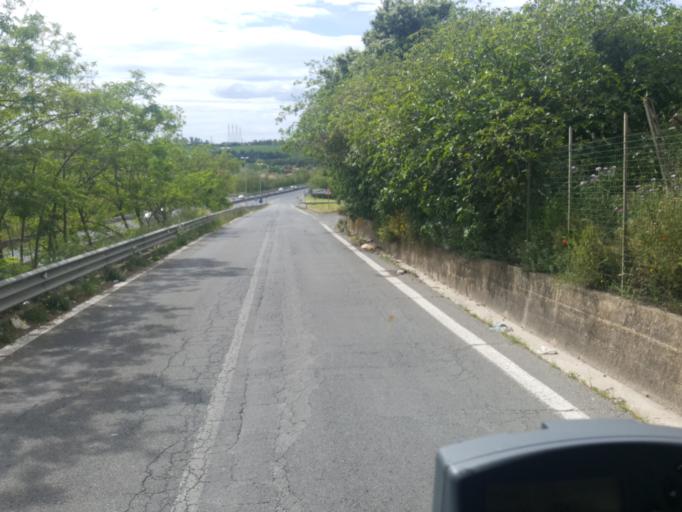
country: IT
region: Latium
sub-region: Citta metropolitana di Roma Capitale
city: La Massimina-Casal Lumbroso
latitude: 41.8826
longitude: 12.3437
